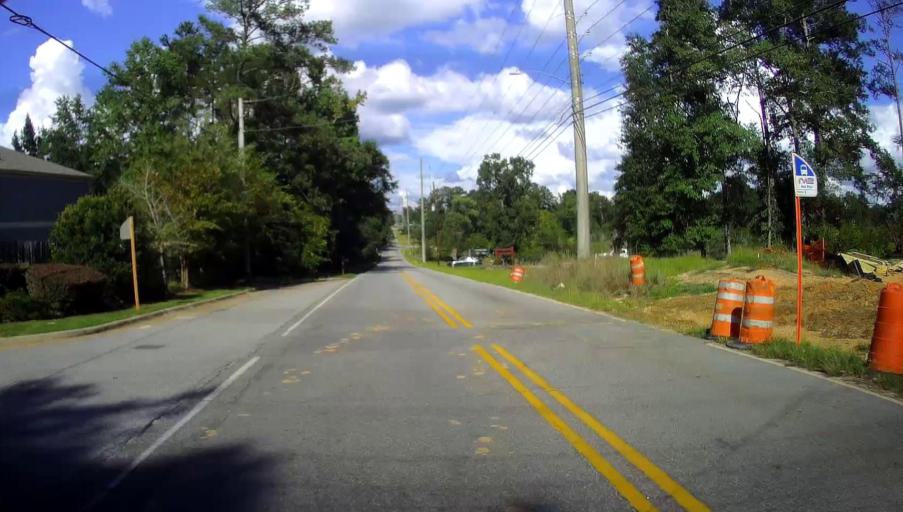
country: US
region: Georgia
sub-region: Muscogee County
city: Columbus
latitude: 32.5485
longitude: -84.8867
